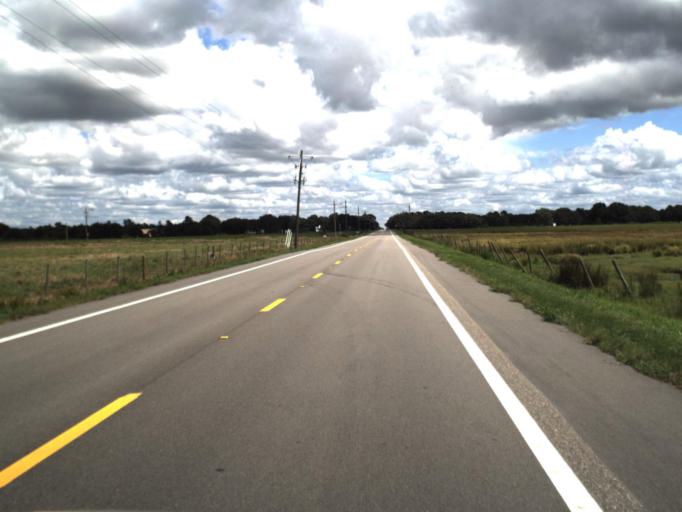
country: US
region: Florida
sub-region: Polk County
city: Crooked Lake Park
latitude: 27.7334
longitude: -81.6489
